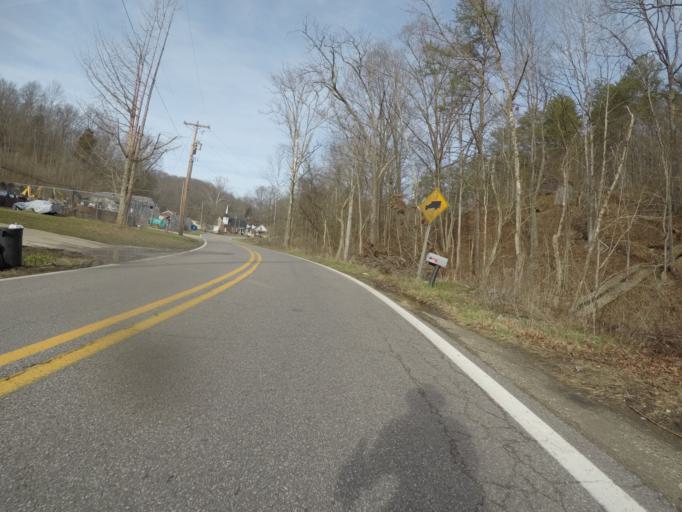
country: US
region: West Virginia
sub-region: Cabell County
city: Pea Ridge
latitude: 38.3634
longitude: -82.3728
